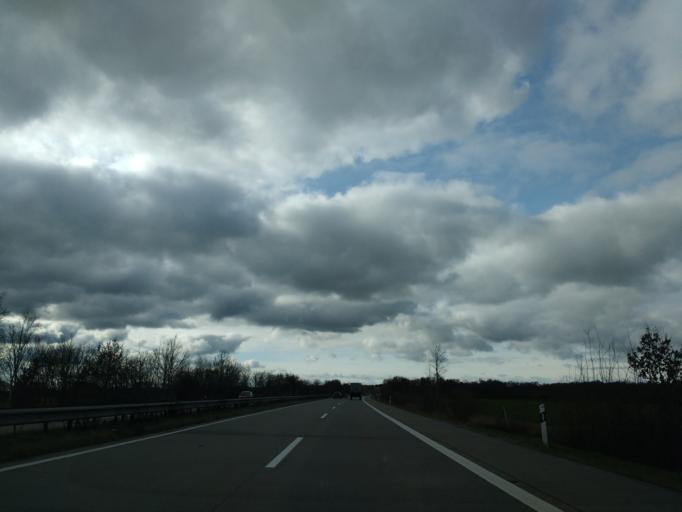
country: DE
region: Lower Saxony
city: Midlum
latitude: 53.7693
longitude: 8.6994
